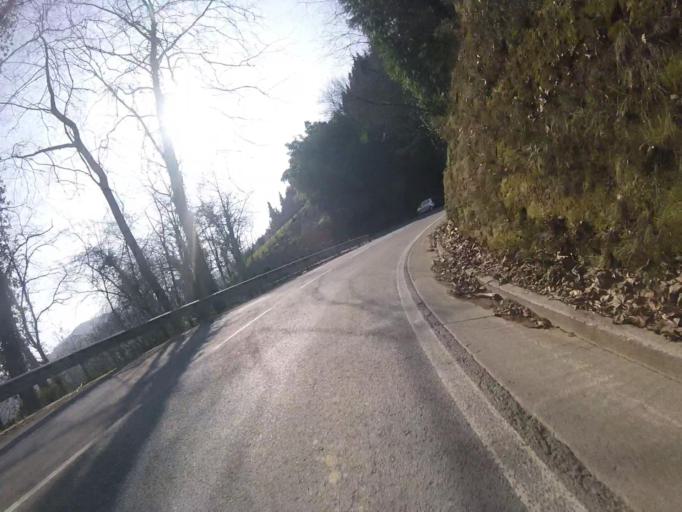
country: ES
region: Navarre
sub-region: Provincia de Navarra
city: Bera
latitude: 43.2940
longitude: -1.6905
